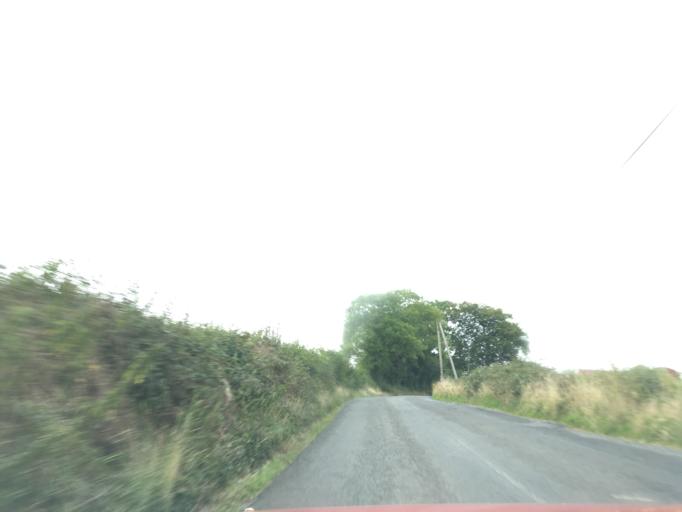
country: IE
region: Munster
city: Cashel
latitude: 52.4682
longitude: -7.8419
